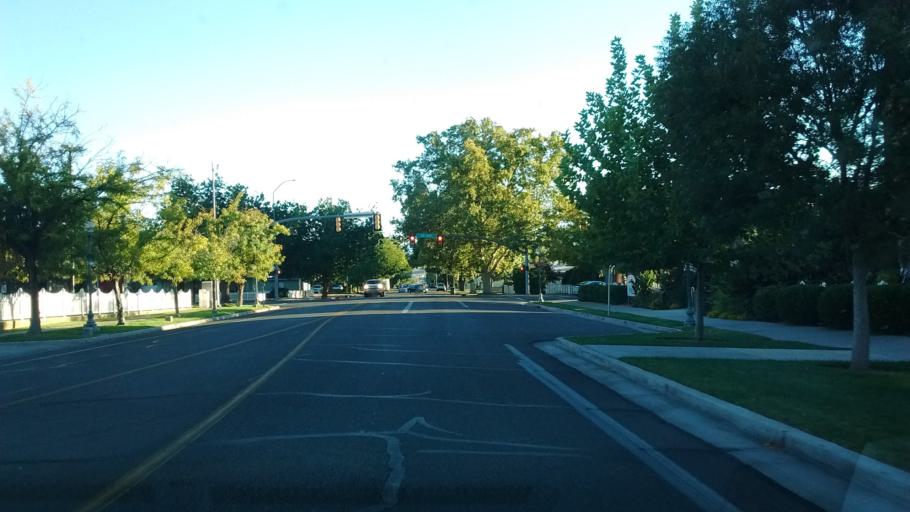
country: US
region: Utah
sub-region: Washington County
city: Saint George
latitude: 37.1072
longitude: -113.5833
